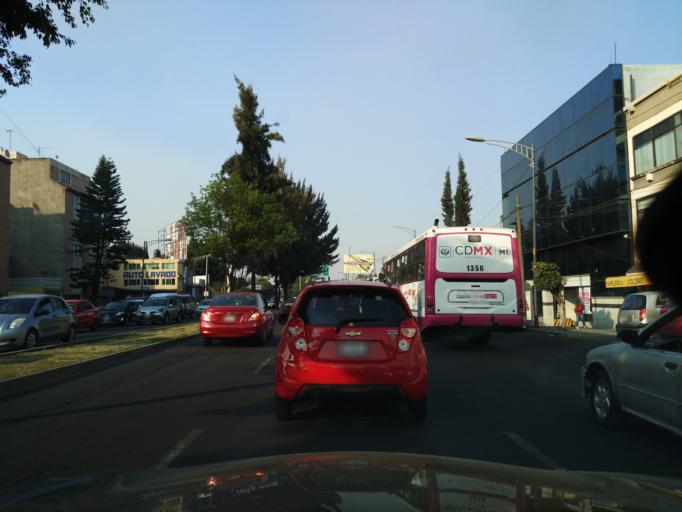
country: MX
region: Mexico City
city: Xochimilco
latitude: 19.3048
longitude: -99.1123
